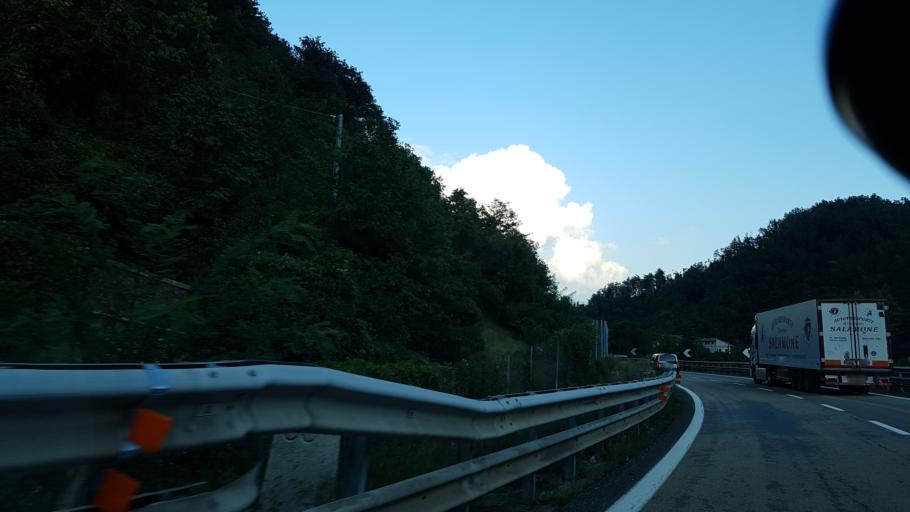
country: IT
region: Liguria
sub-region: Provincia di Genova
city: Isola del Cantone
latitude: 44.6518
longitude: 8.9492
